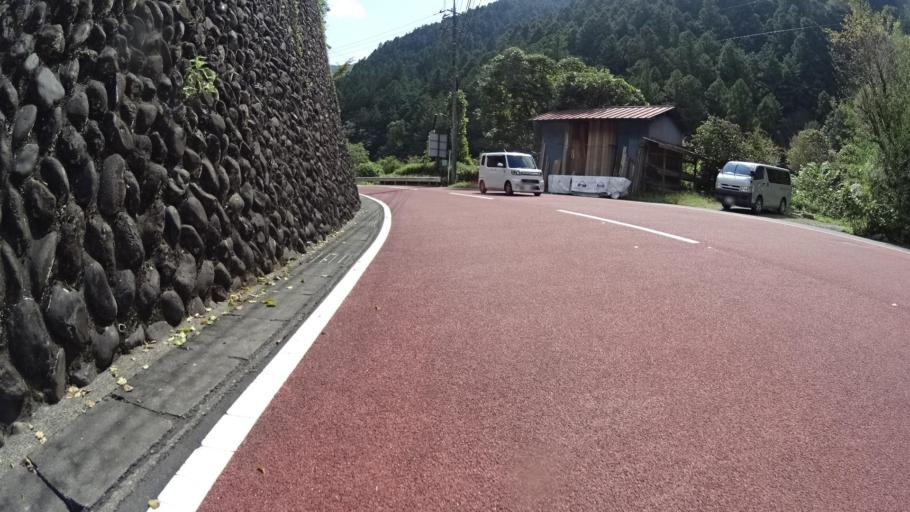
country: JP
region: Tokyo
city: Itsukaichi
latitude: 35.7395
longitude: 139.1389
